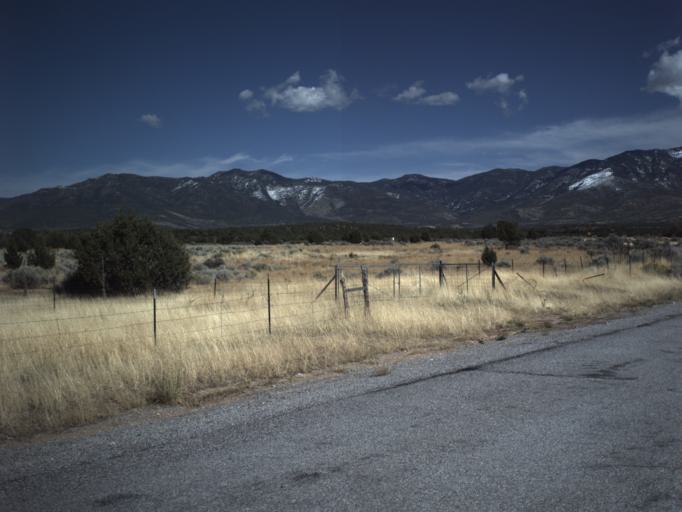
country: US
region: Utah
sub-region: Millard County
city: Fillmore
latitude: 39.0815
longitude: -112.2740
